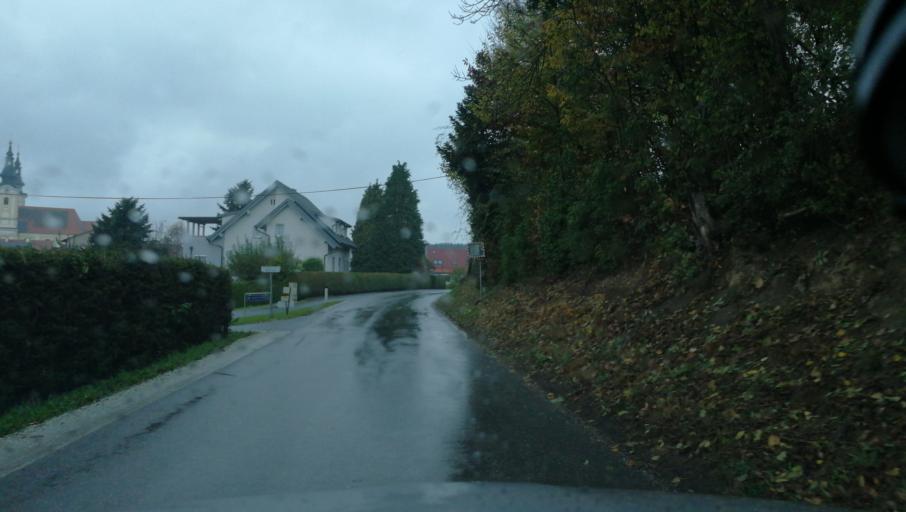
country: AT
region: Styria
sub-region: Politischer Bezirk Leibnitz
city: Sankt Veit am Vogau
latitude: 46.7466
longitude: 15.6302
